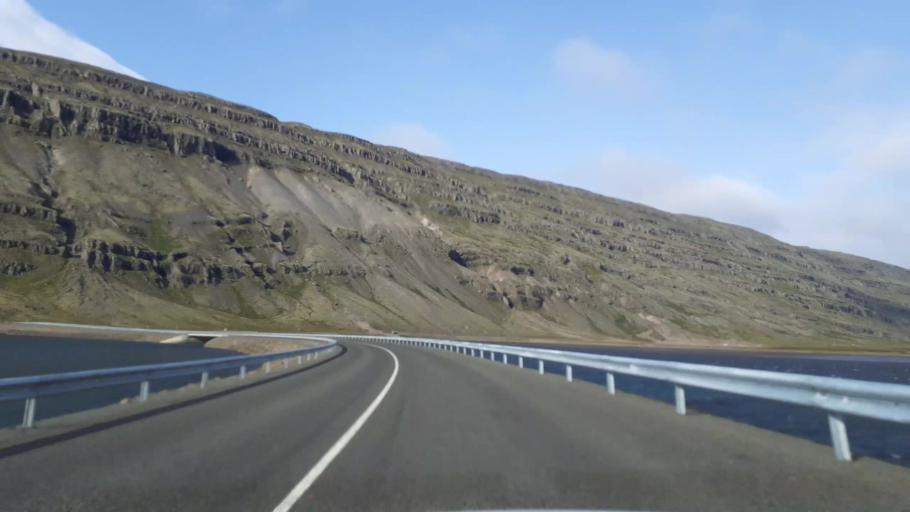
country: IS
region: East
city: Reydarfjoerdur
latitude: 64.7899
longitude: -14.4848
